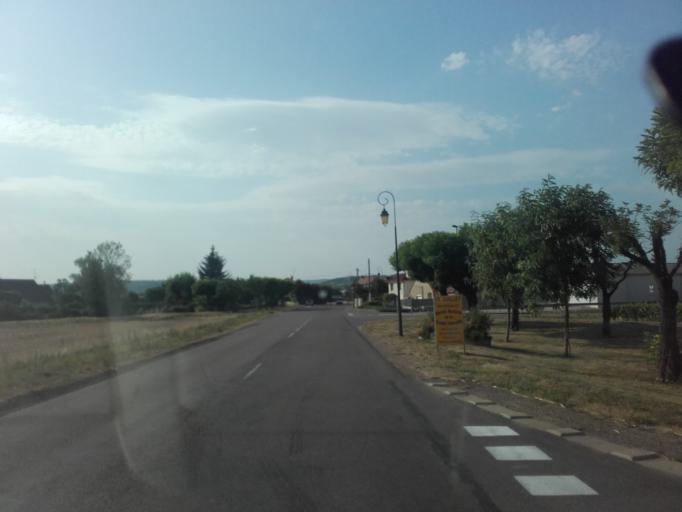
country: FR
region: Bourgogne
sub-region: Departement de la Cote-d'Or
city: Meursault
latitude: 46.9687
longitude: 4.7904
